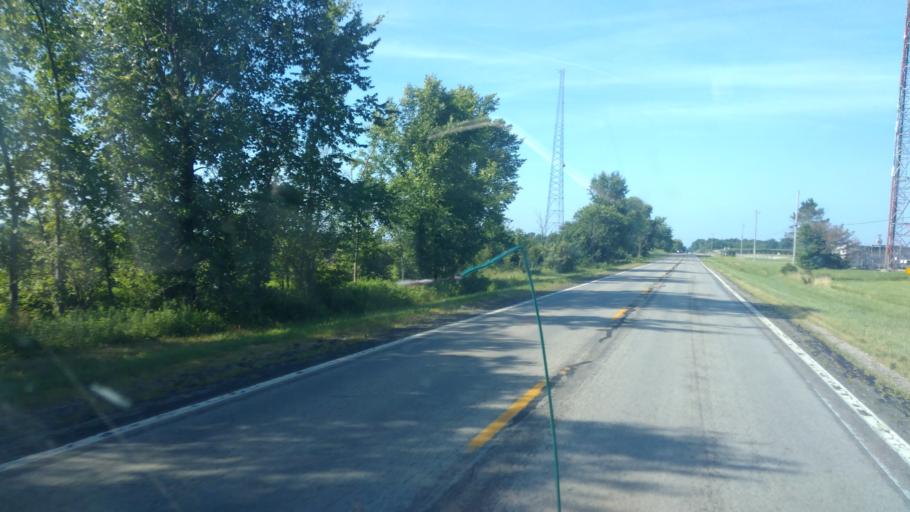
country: US
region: Ohio
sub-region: Delaware County
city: Ashley
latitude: 40.3469
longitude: -82.9960
